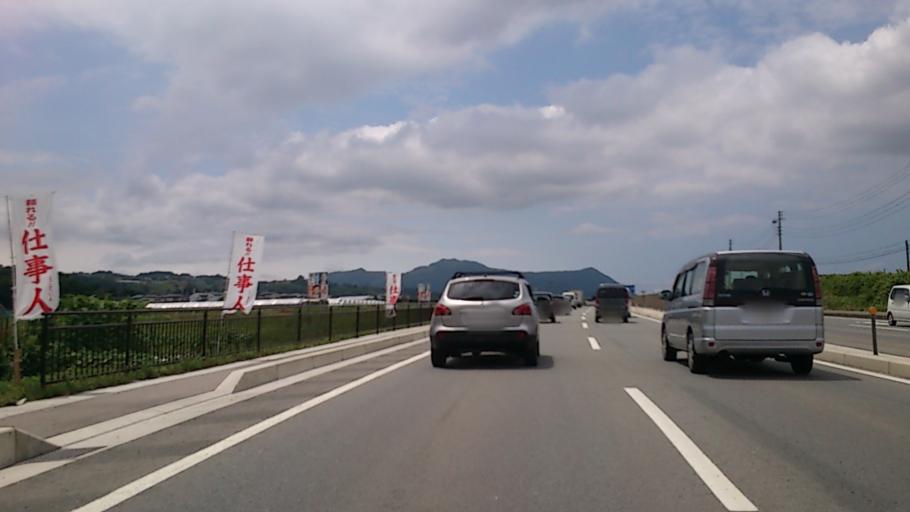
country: JP
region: Yamagata
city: Kaminoyama
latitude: 38.1983
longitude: 140.3146
